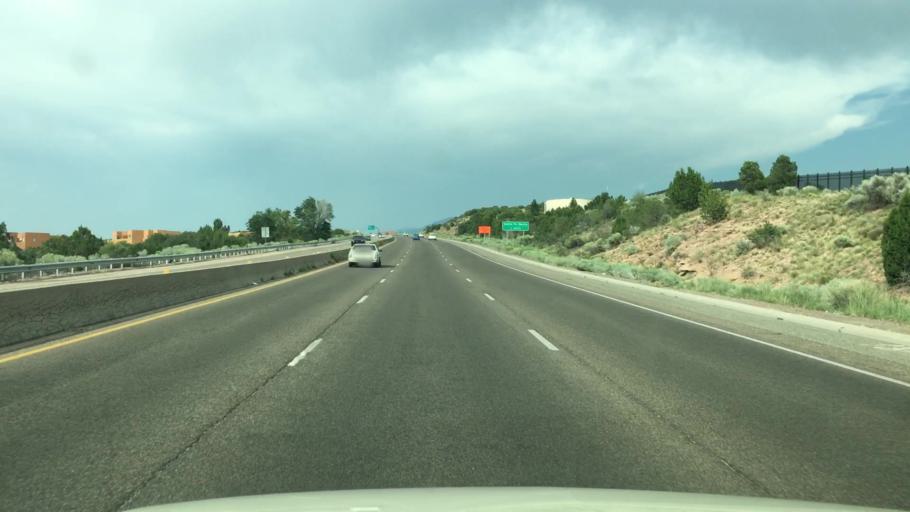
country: US
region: New Mexico
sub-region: Santa Fe County
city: Santa Fe
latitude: 35.7018
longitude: -105.9488
